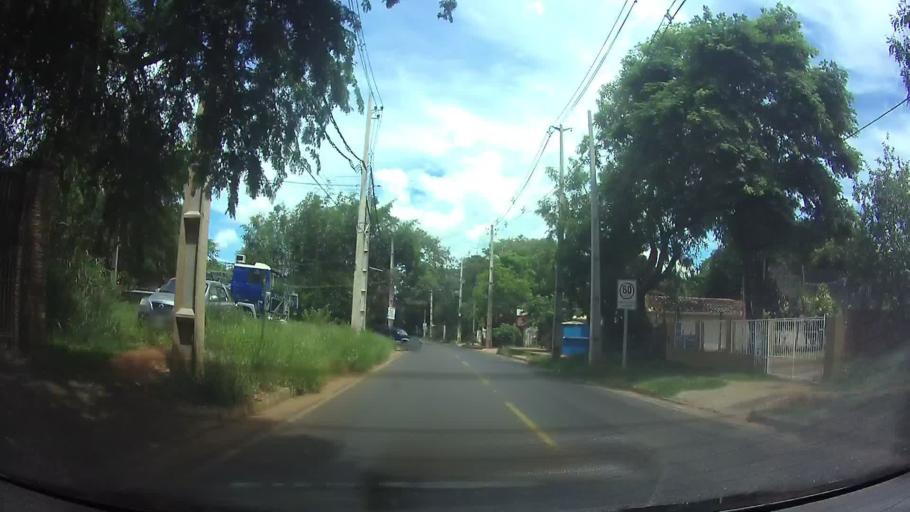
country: PY
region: Central
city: San Lorenzo
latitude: -25.3231
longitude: -57.5119
